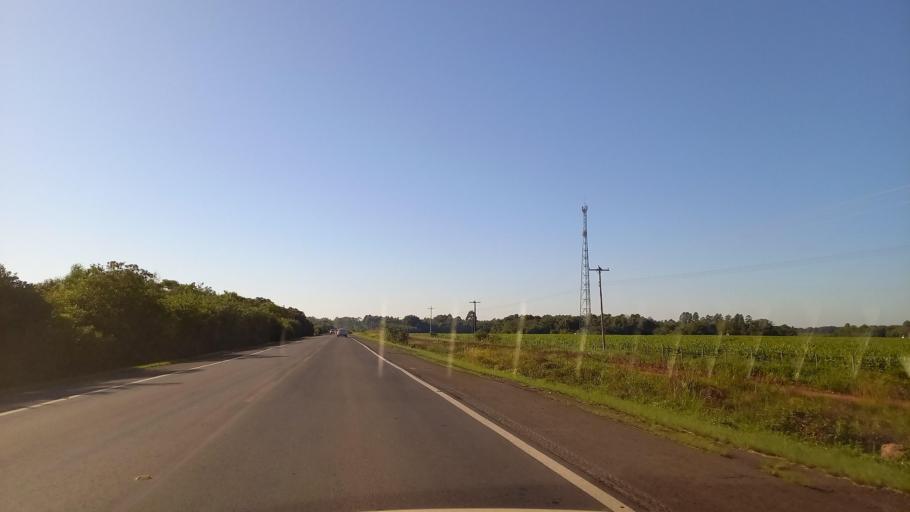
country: BR
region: Rio Grande do Sul
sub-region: Venancio Aires
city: Venancio Aires
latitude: -29.6666
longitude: -52.0483
